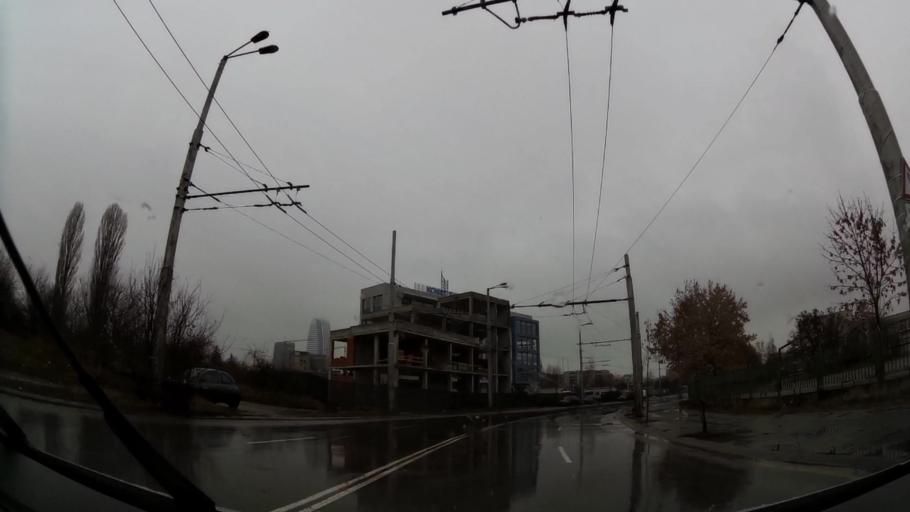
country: BG
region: Sofia-Capital
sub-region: Stolichna Obshtina
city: Sofia
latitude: 42.6434
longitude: 23.4052
